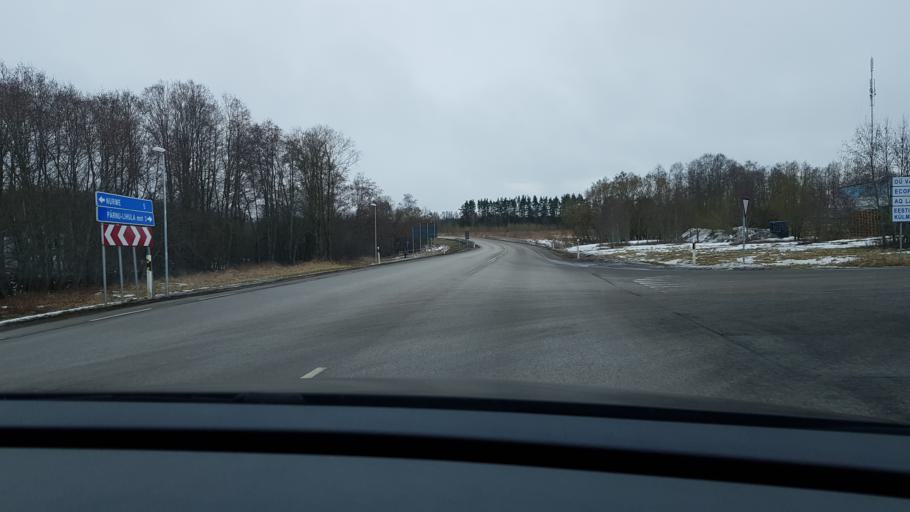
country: EE
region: Paernumaa
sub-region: Sauga vald
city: Sauga
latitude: 58.4256
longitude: 24.4401
